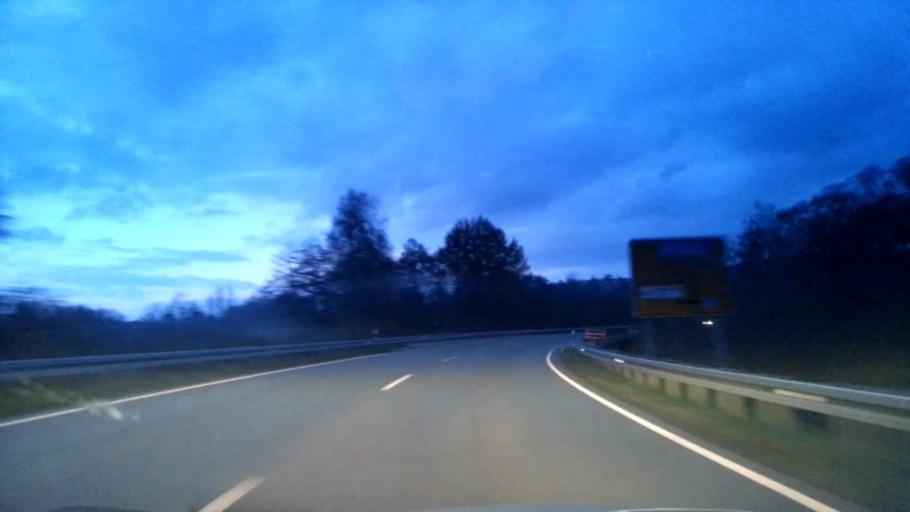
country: DE
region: Bavaria
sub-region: Upper Franconia
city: Seybothenreuth
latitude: 49.9372
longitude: 11.7388
